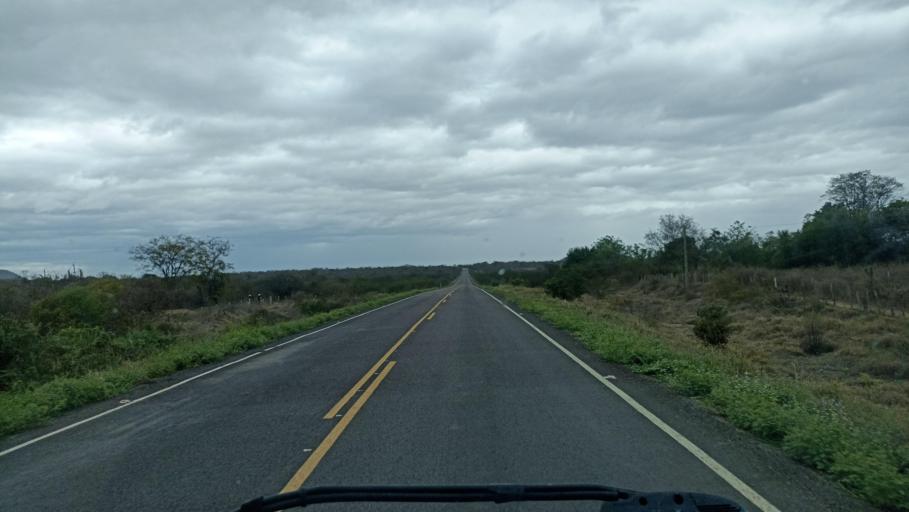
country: BR
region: Bahia
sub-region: Iacu
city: Iacu
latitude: -12.9725
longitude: -40.5043
